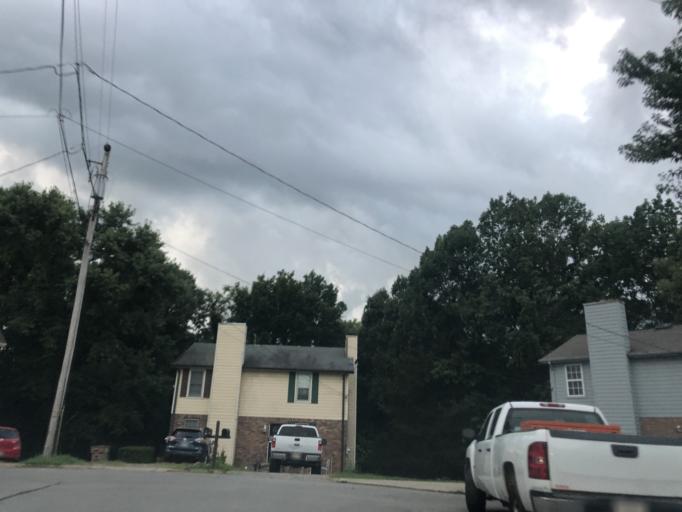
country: US
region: Tennessee
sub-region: Davidson County
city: Lakewood
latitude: 36.1502
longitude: -86.6364
